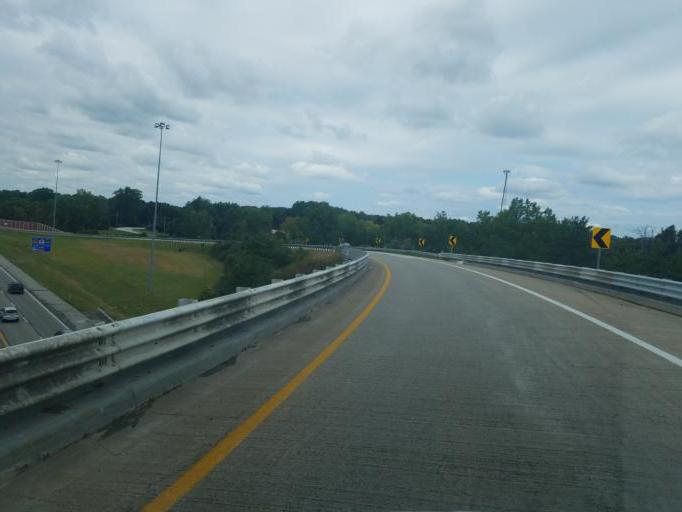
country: US
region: Ohio
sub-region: Lake County
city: Fairport Harbor
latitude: 41.7221
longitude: -81.2824
